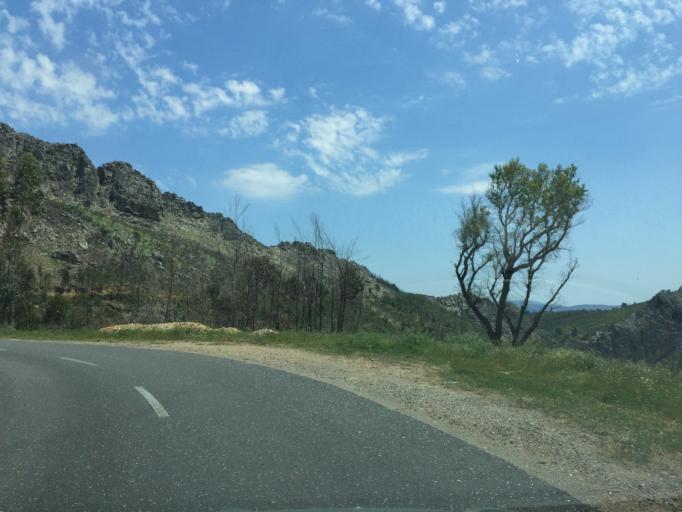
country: PT
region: Coimbra
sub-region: Pampilhosa da Serra
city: Pampilhosa da Serra
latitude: 40.0903
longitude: -7.8698
